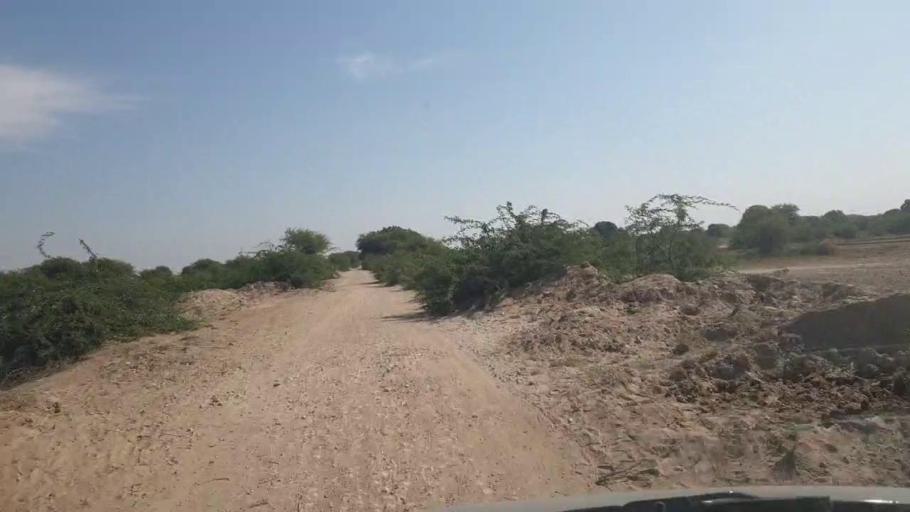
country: PK
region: Sindh
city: Digri
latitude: 24.9526
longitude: 69.1444
